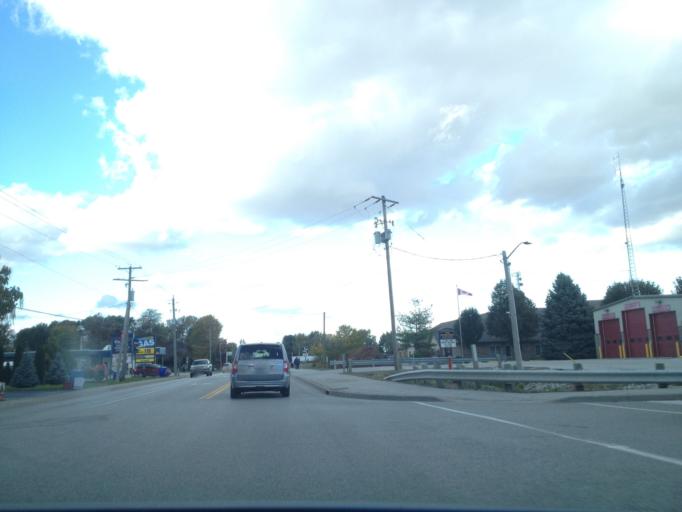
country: CA
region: Ontario
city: Amherstburg
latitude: 42.0487
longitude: -82.7387
